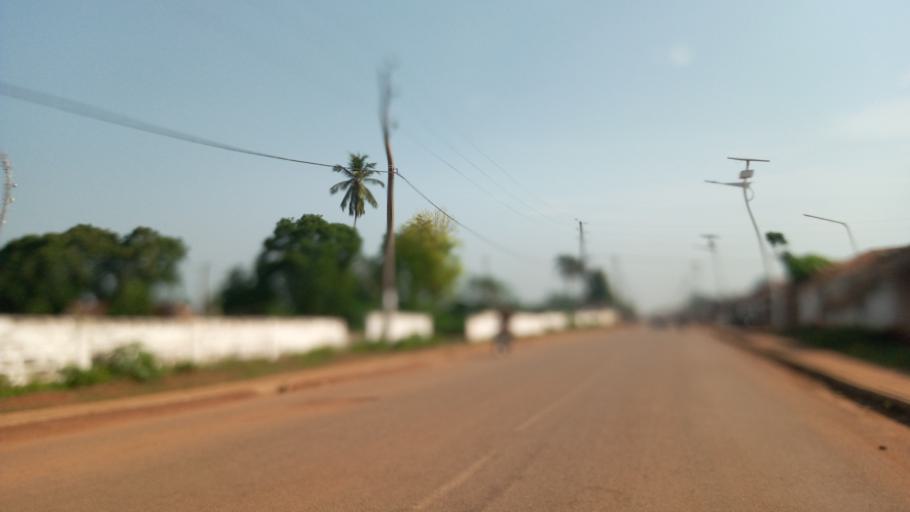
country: BJ
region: Queme
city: Porto-Novo
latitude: 6.5517
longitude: 2.6551
